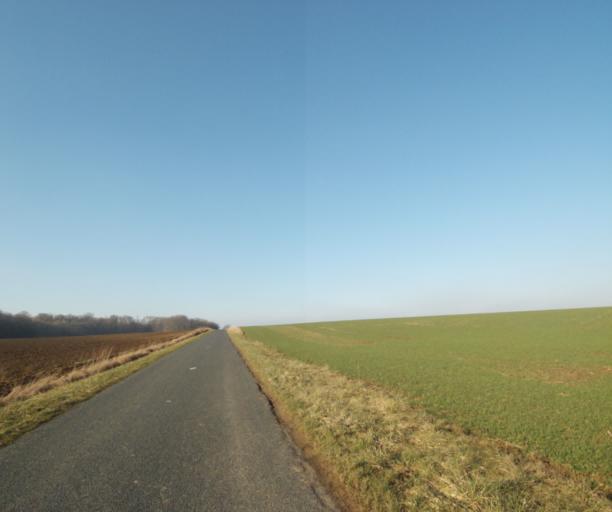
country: FR
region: Champagne-Ardenne
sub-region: Departement de la Haute-Marne
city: Chevillon
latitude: 48.4856
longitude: 5.0843
